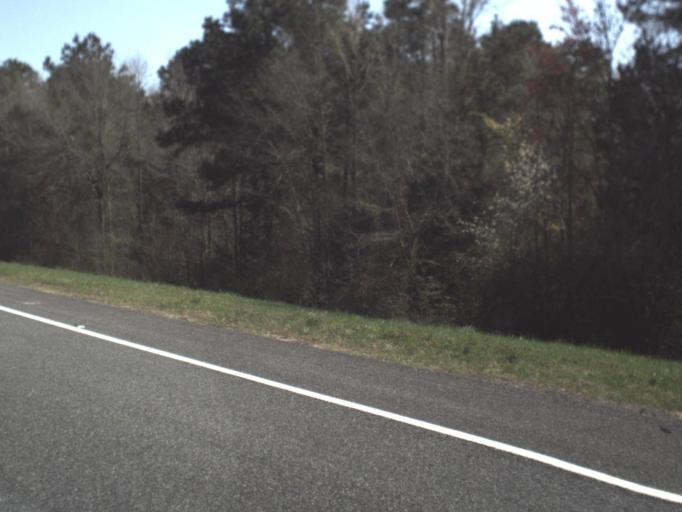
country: US
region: Florida
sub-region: Jackson County
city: Marianna
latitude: 30.7554
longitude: -85.2777
